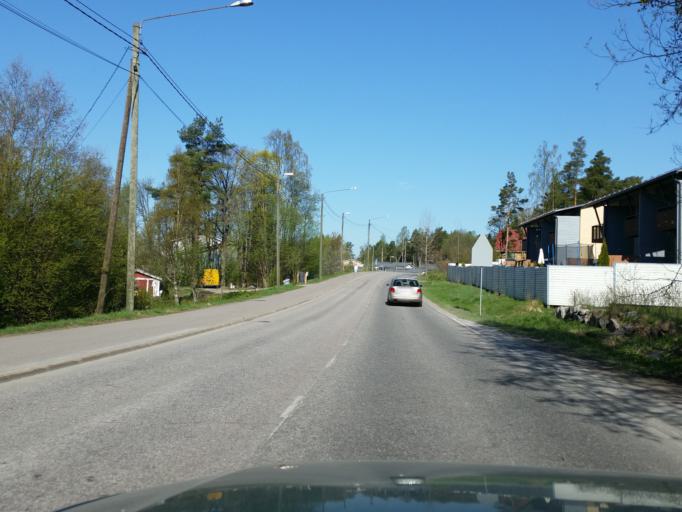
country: FI
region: Uusimaa
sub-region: Helsinki
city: Kirkkonummi
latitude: 60.1338
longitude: 24.4264
